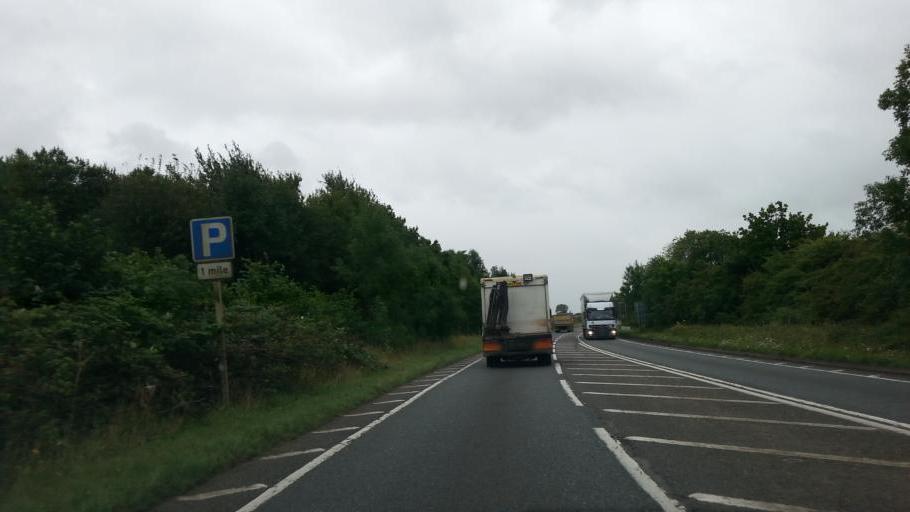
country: GB
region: England
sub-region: Northamptonshire
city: Oundle
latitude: 52.4518
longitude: -0.4622
